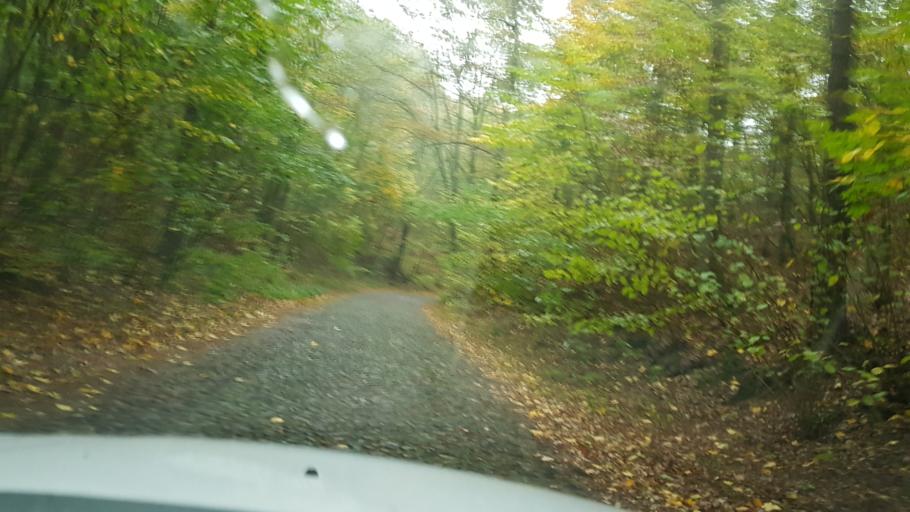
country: PL
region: West Pomeranian Voivodeship
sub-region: Powiat mysliborski
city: Barlinek
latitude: 53.0339
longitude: 15.2356
